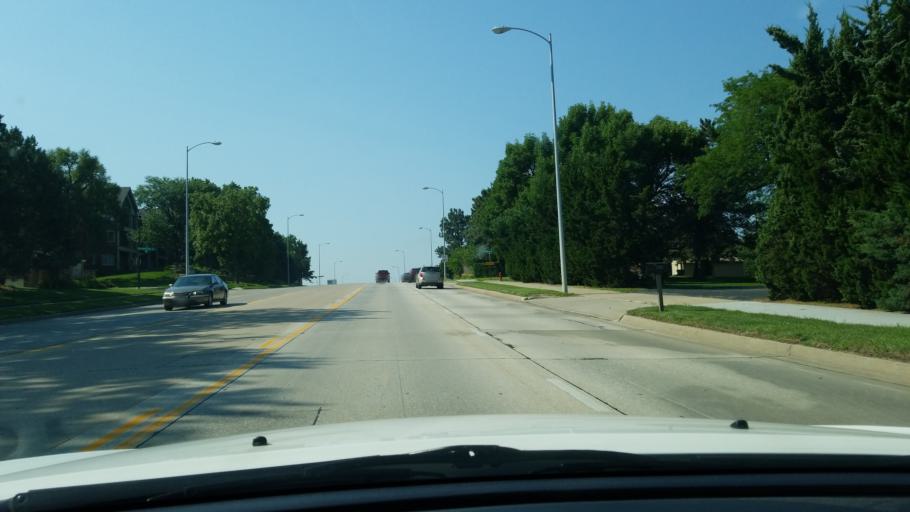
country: US
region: Nebraska
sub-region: Lancaster County
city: Lincoln
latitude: 40.7879
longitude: -96.6252
